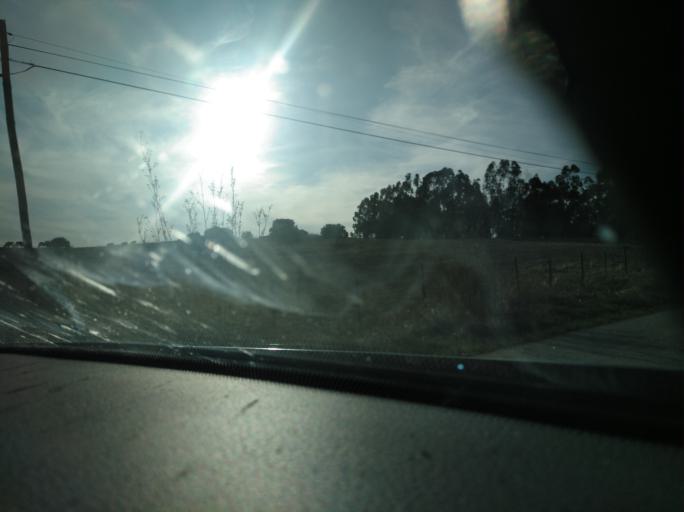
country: PT
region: Evora
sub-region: Borba
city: Borba
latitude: 38.9261
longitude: -7.4325
